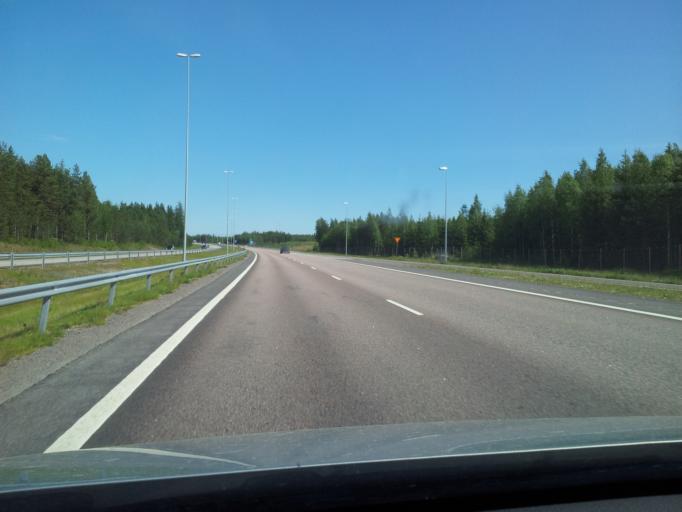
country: FI
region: Uusimaa
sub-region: Loviisa
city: Lovisa
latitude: 60.4618
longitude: 26.1489
